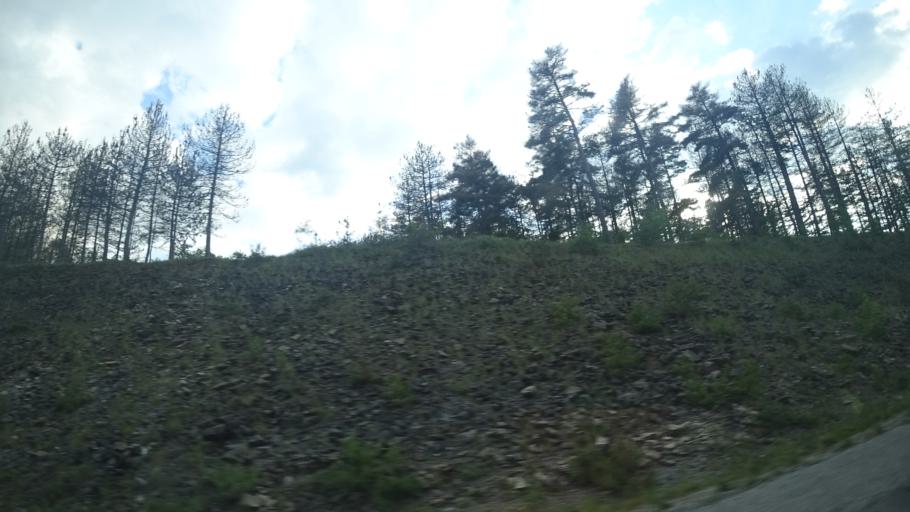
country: FR
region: Midi-Pyrenees
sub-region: Departement de l'Aveyron
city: Millau
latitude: 44.1984
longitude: 3.0181
